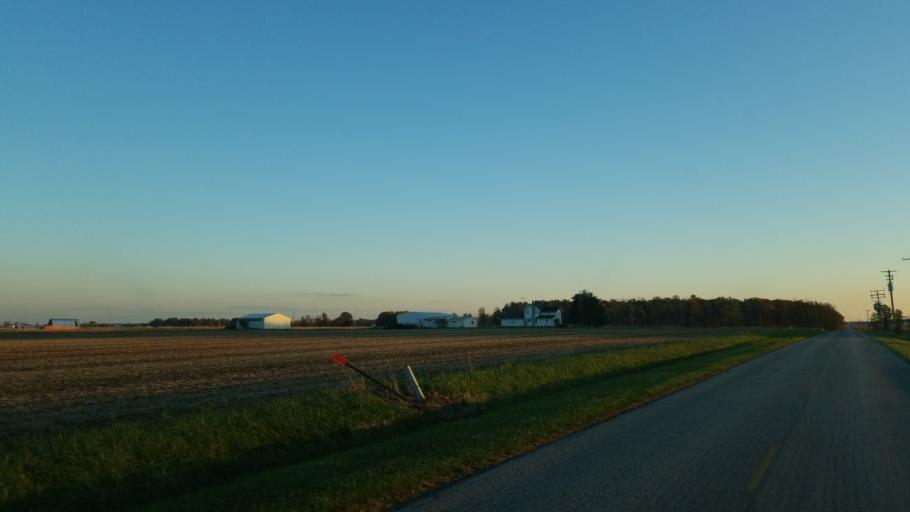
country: US
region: Ohio
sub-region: Huron County
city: Bellevue
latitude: 41.1632
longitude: -82.8805
